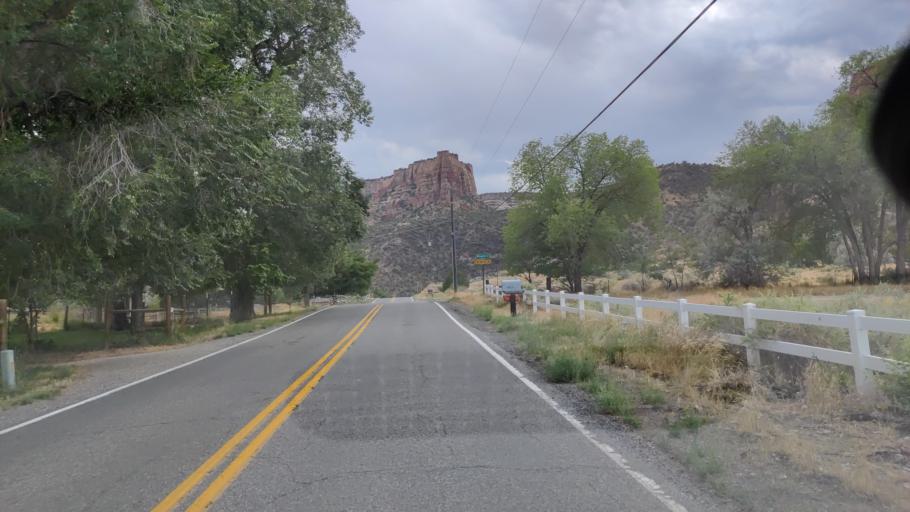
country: US
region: Colorado
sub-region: Mesa County
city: Redlands
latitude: 39.0957
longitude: -108.6920
